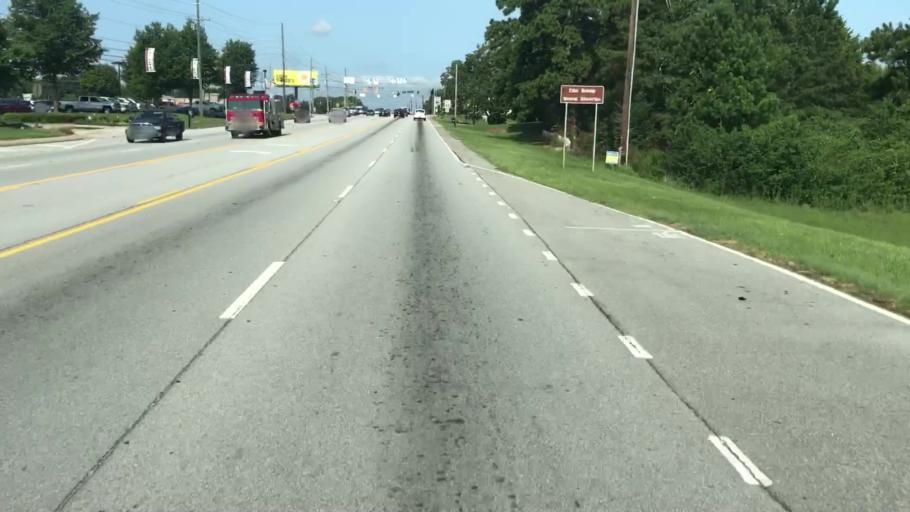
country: US
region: Georgia
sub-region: Walton County
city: Loganville
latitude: 33.8325
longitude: -83.8794
